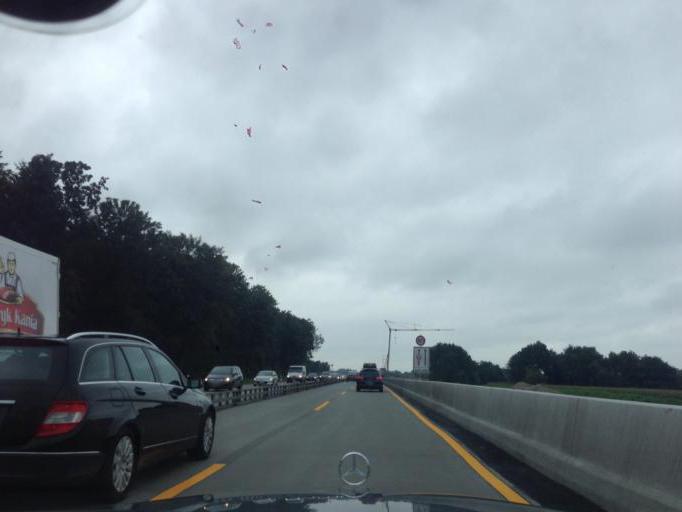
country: DE
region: Schleswig-Holstein
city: Grossenaspe
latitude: 53.9743
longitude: 9.9473
